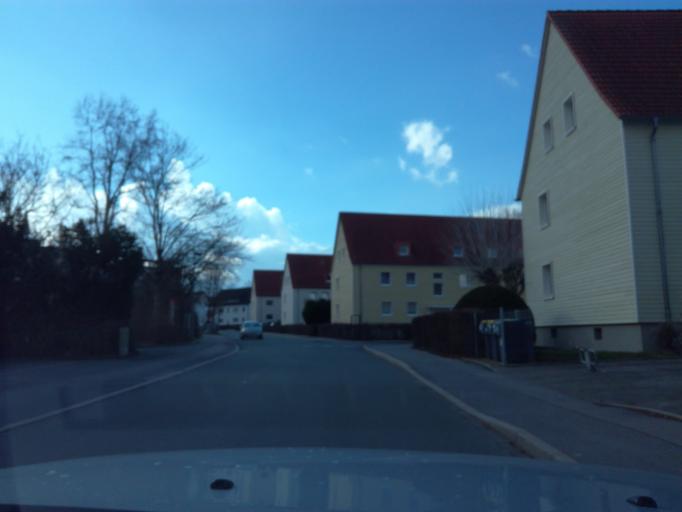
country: DE
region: North Rhine-Westphalia
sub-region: Regierungsbezirk Arnsberg
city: Menden
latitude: 51.4341
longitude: 7.7615
